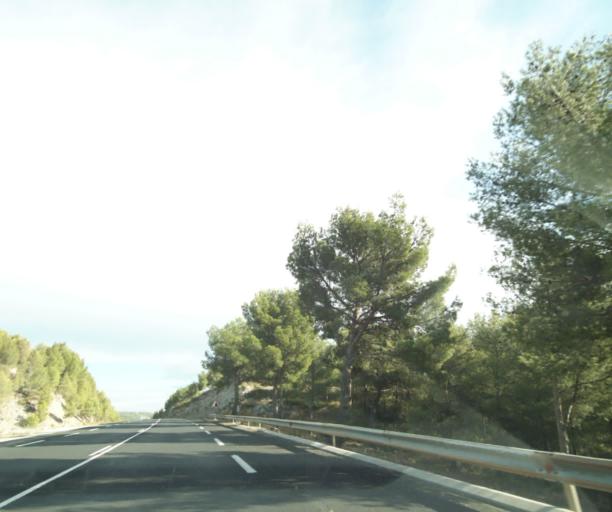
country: FR
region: Provence-Alpes-Cote d'Azur
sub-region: Departement des Bouches-du-Rhone
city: Sausset-les-Pins
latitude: 43.3446
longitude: 5.0824
